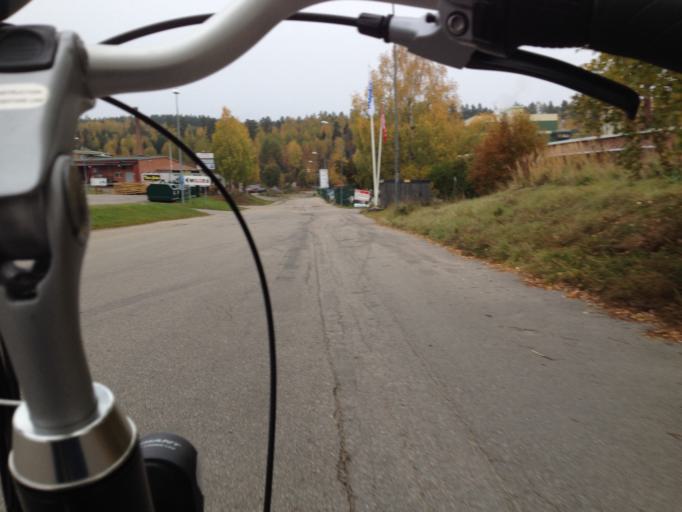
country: SE
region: Gaevleborg
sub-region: Bollnas Kommun
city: Bollnas
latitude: 61.3434
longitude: 16.3825
